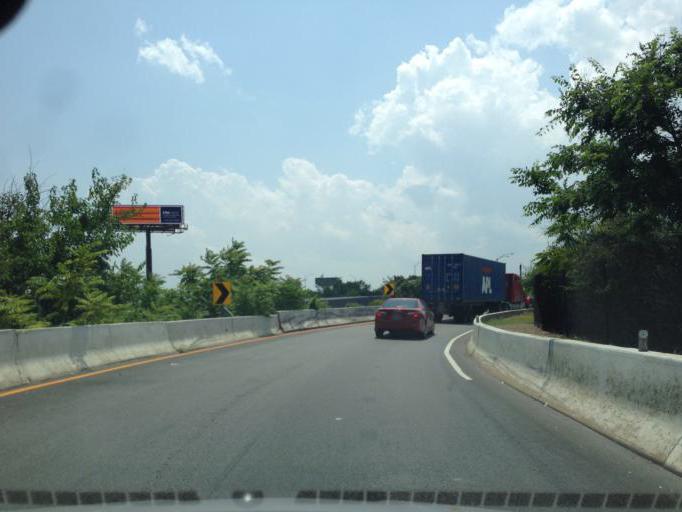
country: US
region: Maryland
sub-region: Baltimore County
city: Dundalk
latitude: 39.2815
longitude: -76.5511
